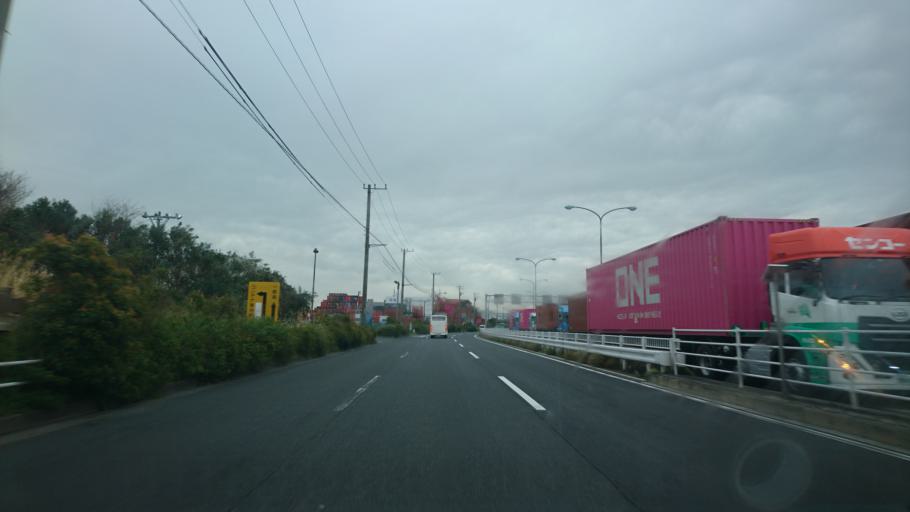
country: JP
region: Kanagawa
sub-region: Kawasaki-shi
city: Kawasaki
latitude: 35.6047
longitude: 139.7605
